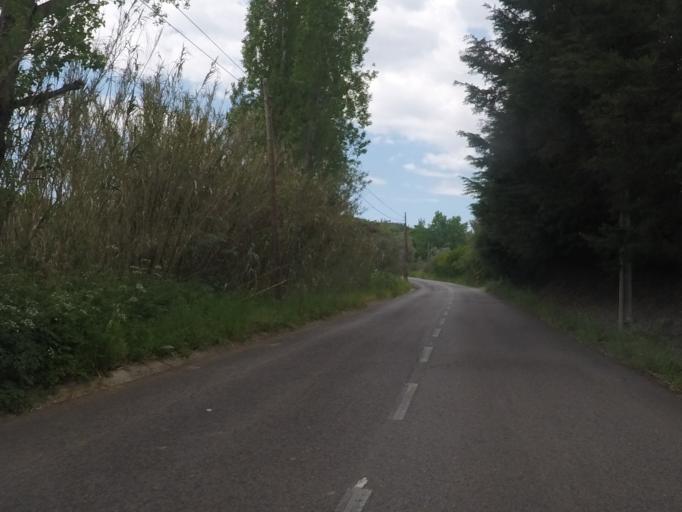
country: PT
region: Setubal
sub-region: Palmela
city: Quinta do Anjo
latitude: 38.5024
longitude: -8.9981
